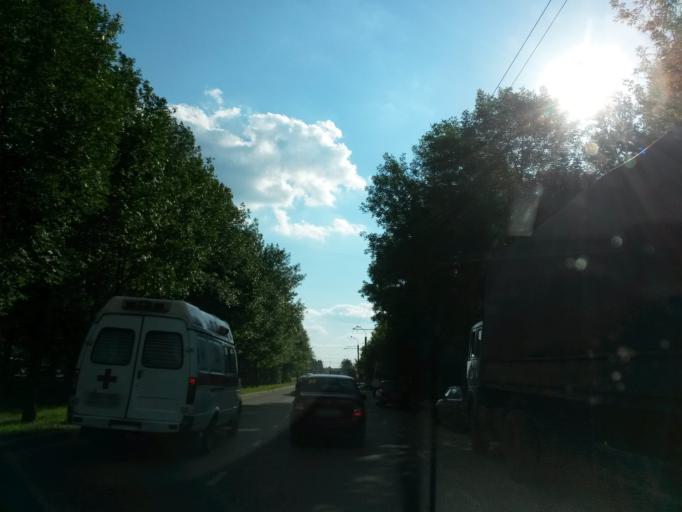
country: RU
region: Ivanovo
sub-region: Gorod Ivanovo
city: Ivanovo
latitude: 56.9613
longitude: 41.0114
